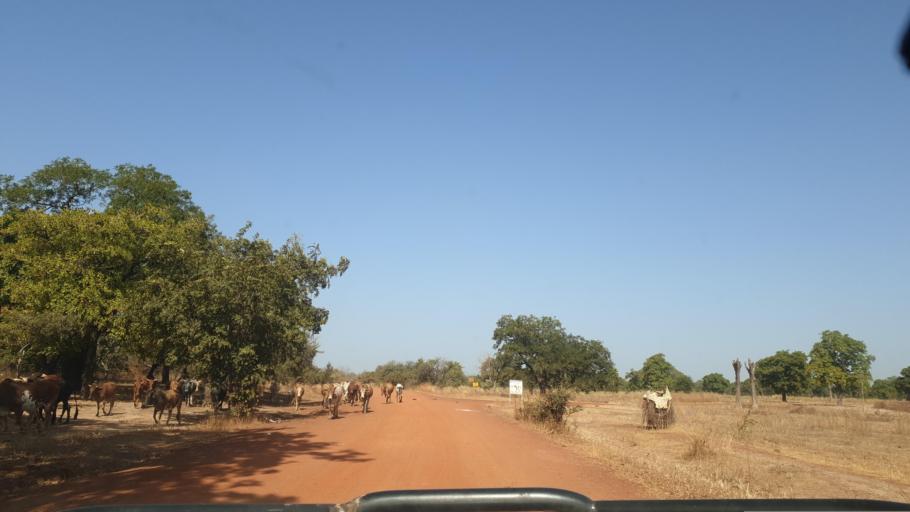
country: ML
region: Sikasso
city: Bougouni
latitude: 11.8158
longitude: -6.9371
